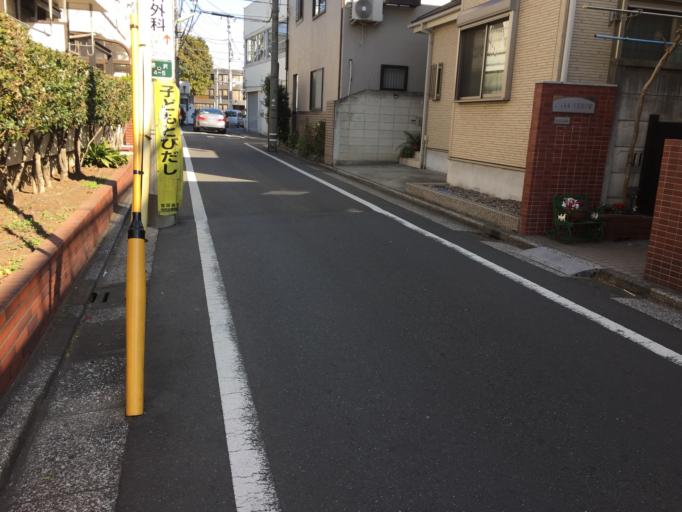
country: JP
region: Tokyo
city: Tokyo
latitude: 35.6308
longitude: 139.6696
